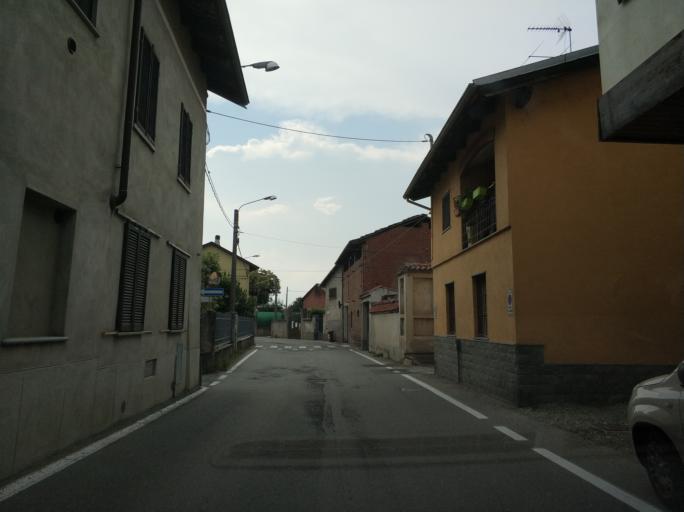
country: IT
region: Piedmont
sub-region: Provincia di Torino
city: Caluso
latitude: 45.3082
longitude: 7.8844
